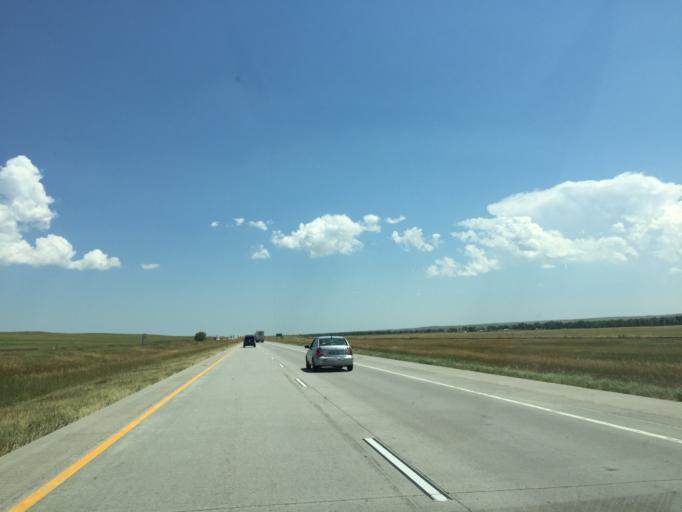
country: US
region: Colorado
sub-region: Lincoln County
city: Limon
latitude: 39.2979
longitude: -103.8070
